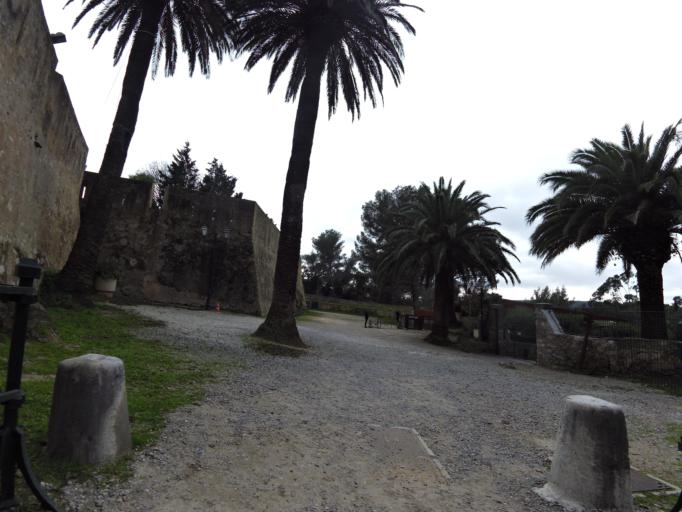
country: FR
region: Provence-Alpes-Cote d'Azur
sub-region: Departement du Var
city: Saint-Tropez
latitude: 43.2720
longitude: 6.6440
